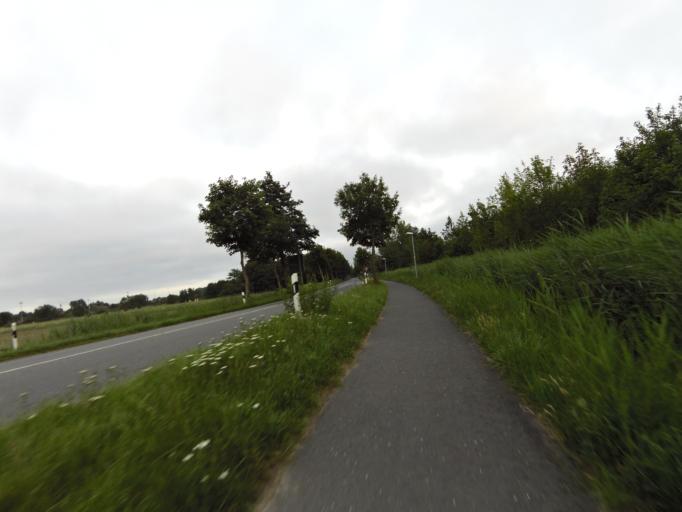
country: DE
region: Lower Saxony
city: Dorum
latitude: 53.6966
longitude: 8.5622
